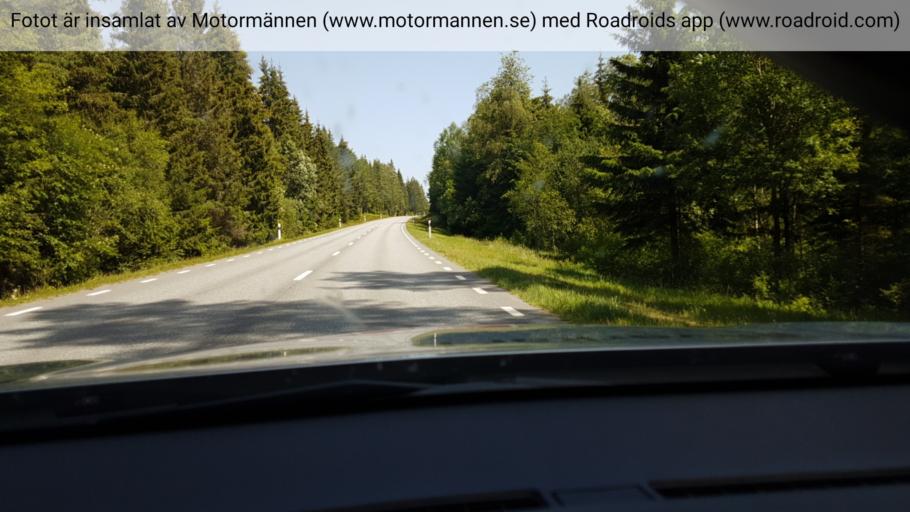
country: SE
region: Joenkoeping
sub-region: Nassjo Kommun
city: Bodafors
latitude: 57.4554
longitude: 14.7322
